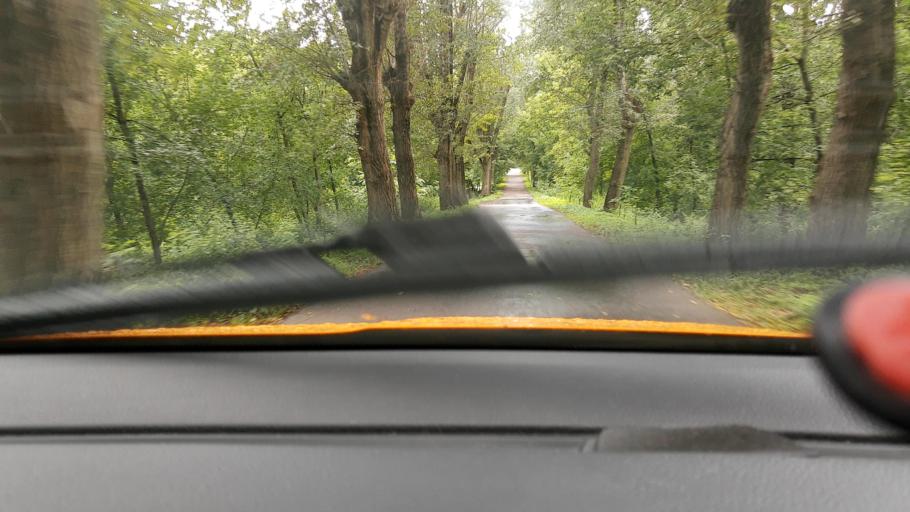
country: RU
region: Moscow
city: Kolomenskoye
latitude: 55.6730
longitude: 37.7037
